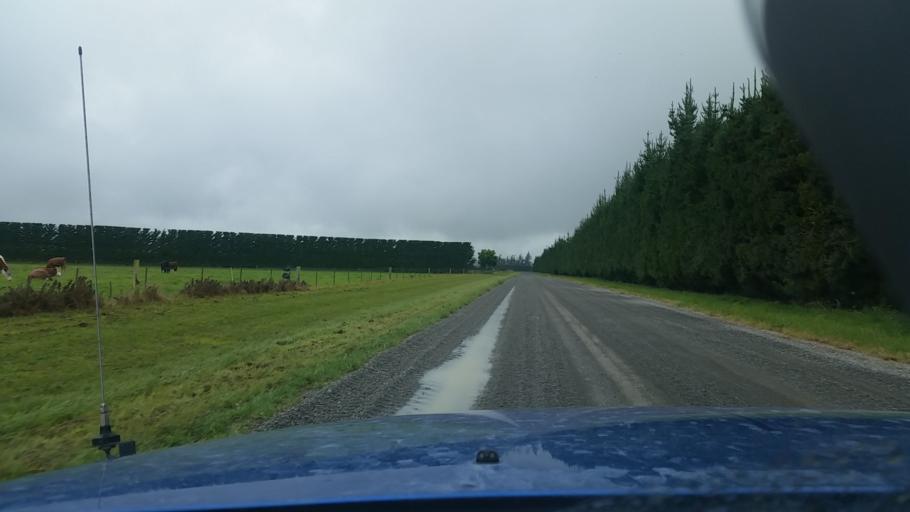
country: NZ
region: Canterbury
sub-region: Ashburton District
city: Methven
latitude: -43.6609
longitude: 171.7979
